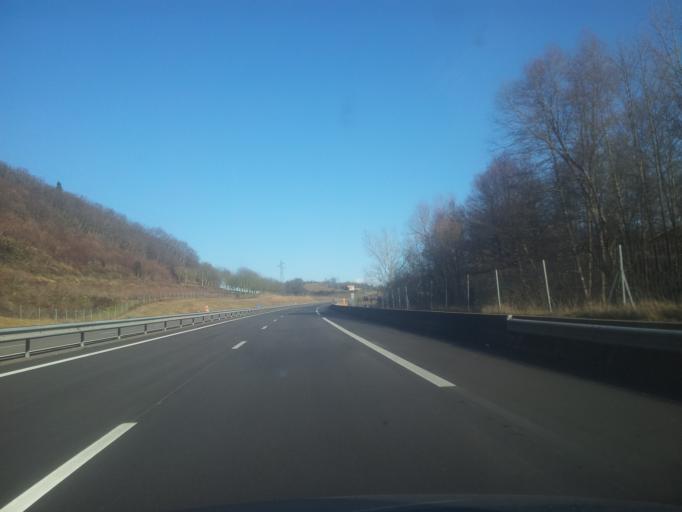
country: FR
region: Rhone-Alpes
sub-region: Departement de l'Isere
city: Saint-Hilaire-du-Rosier
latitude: 45.0969
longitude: 5.2264
